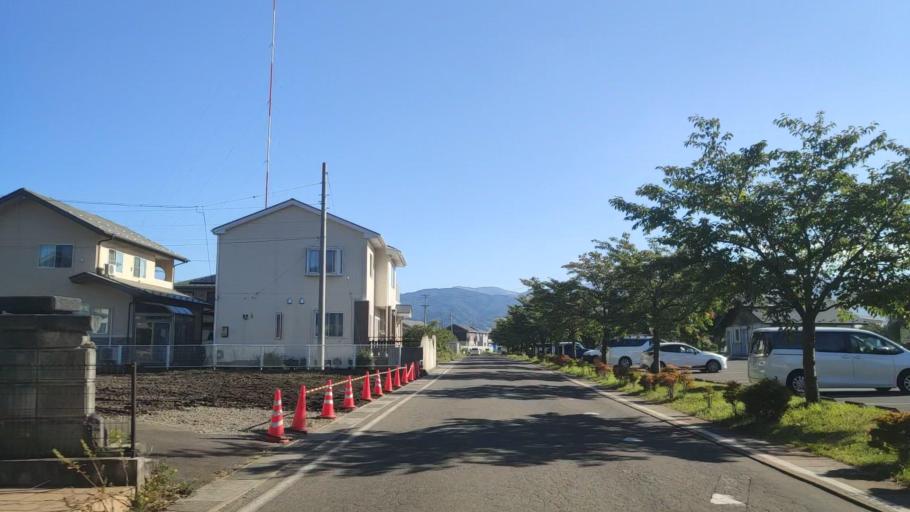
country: JP
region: Nagano
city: Okaya
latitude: 36.0576
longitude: 138.0617
